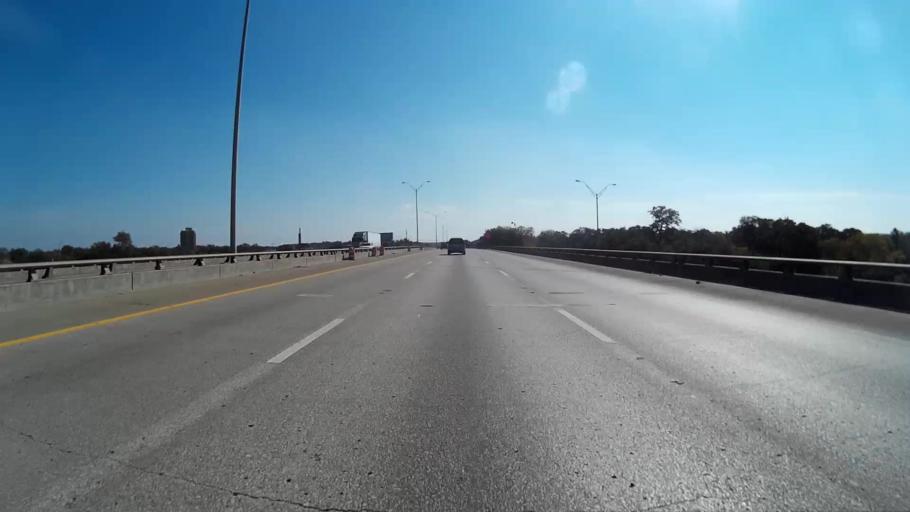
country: US
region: Texas
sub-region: Dallas County
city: Dallas
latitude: 32.7668
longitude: -96.7769
